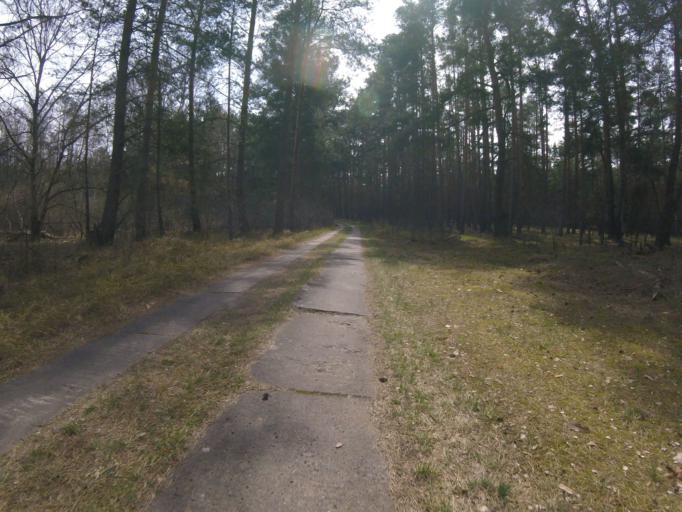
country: DE
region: Brandenburg
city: Schwerin
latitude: 52.1792
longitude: 13.6351
